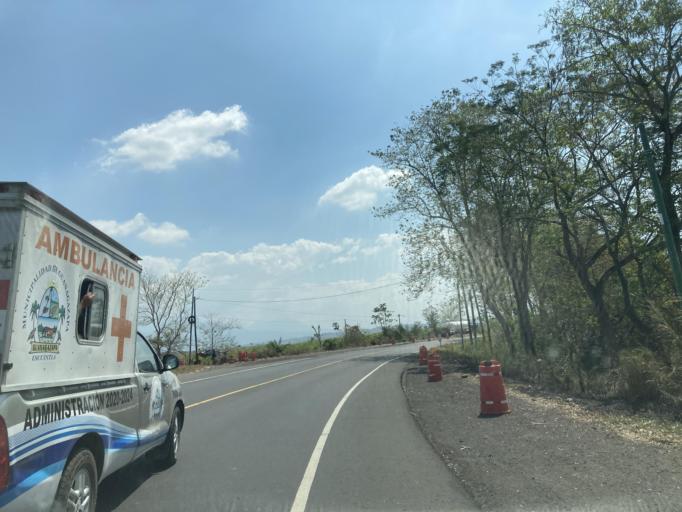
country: GT
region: Escuintla
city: Guanagazapa
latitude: 14.2041
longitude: -90.7059
